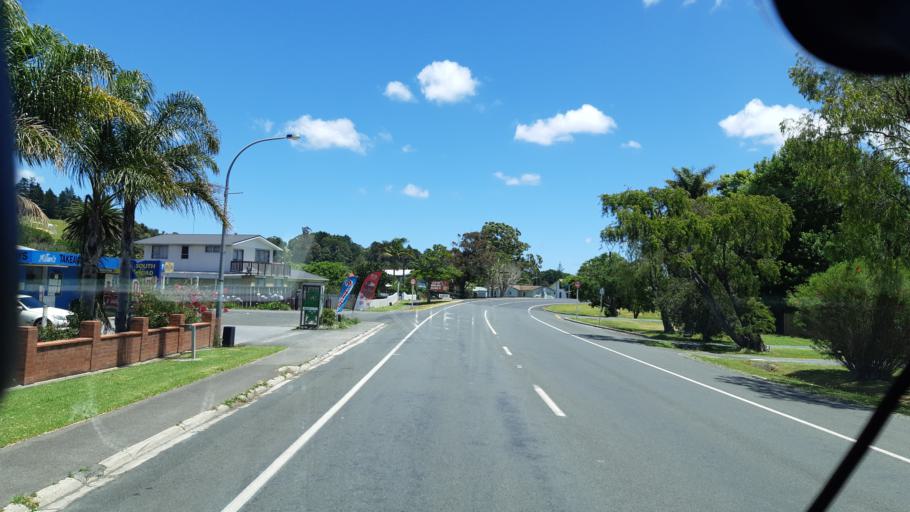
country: NZ
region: Northland
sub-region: Far North District
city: Kaitaia
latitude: -35.1213
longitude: 173.2717
